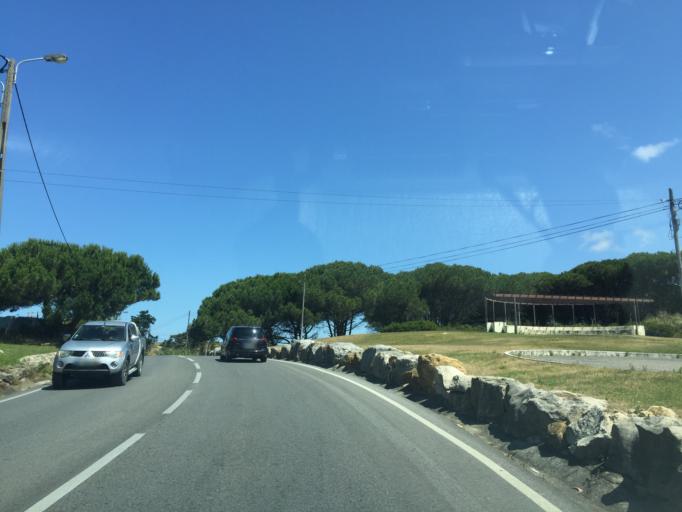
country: PT
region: Lisbon
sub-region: Sintra
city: Sintra
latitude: 38.8223
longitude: -9.4080
